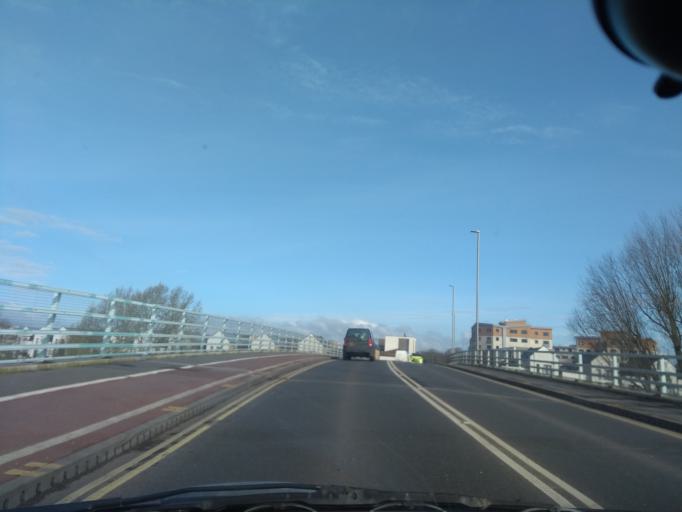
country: GB
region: England
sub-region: Somerset
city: Taunton
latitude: 51.0206
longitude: -3.0942
